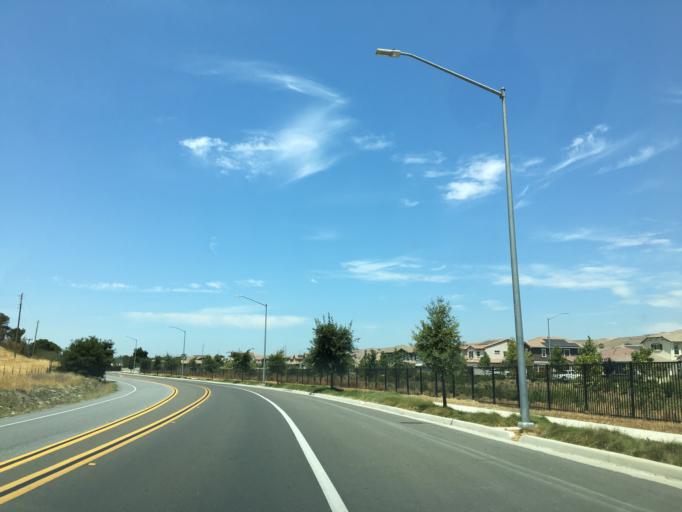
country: US
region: California
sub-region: Santa Clara County
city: Morgan Hill
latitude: 37.1453
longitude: -121.6699
